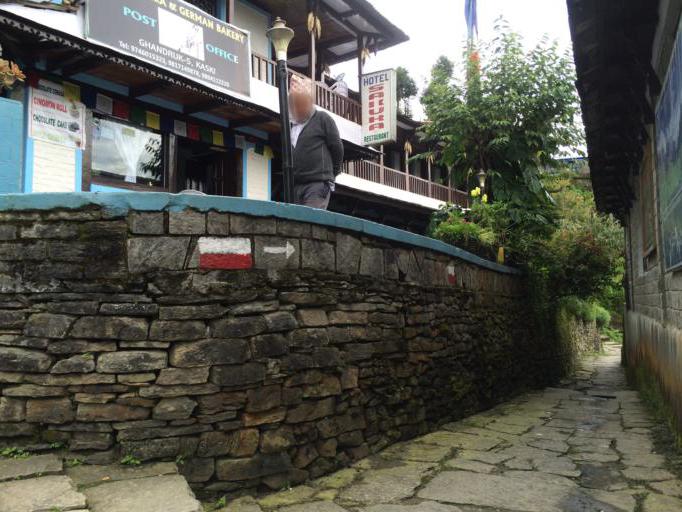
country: NP
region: Western Region
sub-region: Dhawalagiri Zone
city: Chitre
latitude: 28.3748
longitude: 83.8082
